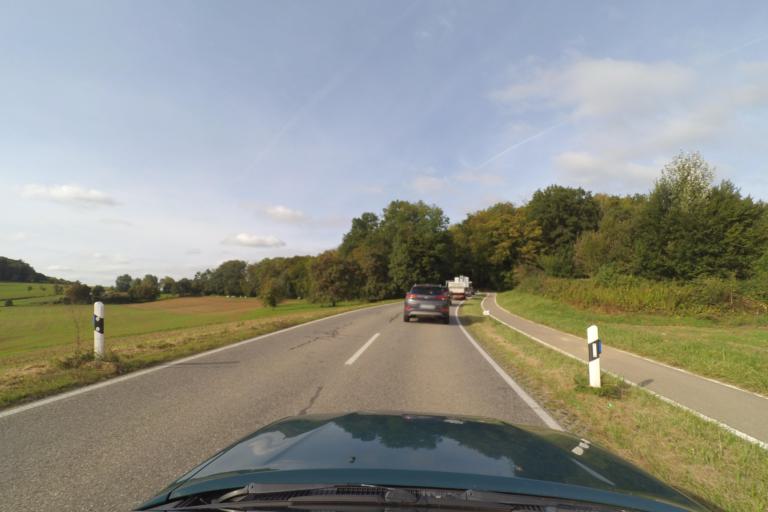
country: DE
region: Baden-Wuerttemberg
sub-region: Freiburg Region
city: Kandern
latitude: 47.7215
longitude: 7.6274
